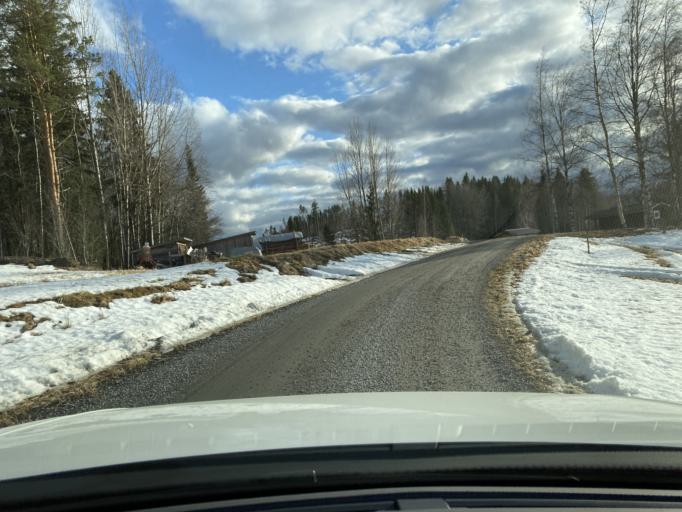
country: FI
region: Pirkanmaa
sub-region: Lounais-Pirkanmaa
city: Mouhijaervi
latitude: 61.4390
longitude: 22.9656
